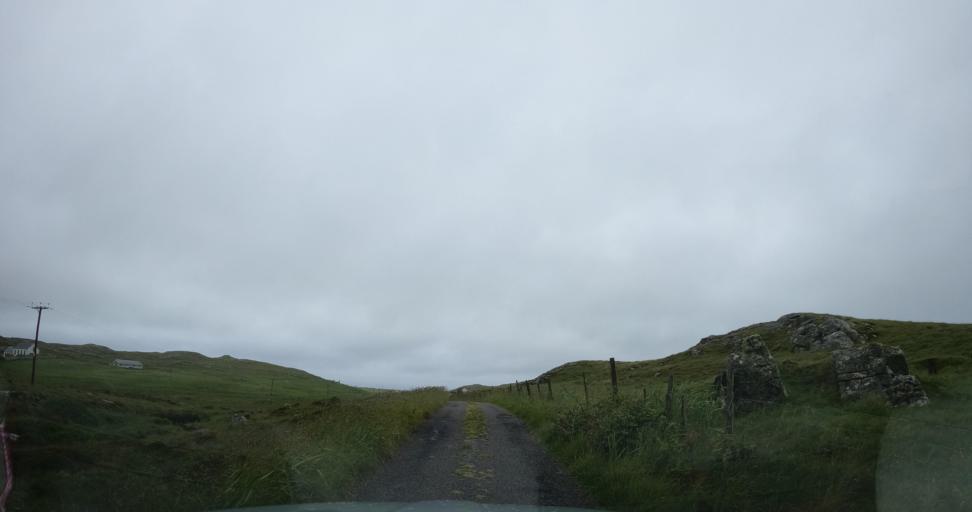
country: GB
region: Scotland
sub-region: Eilean Siar
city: Barra
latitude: 57.0032
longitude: -7.4819
